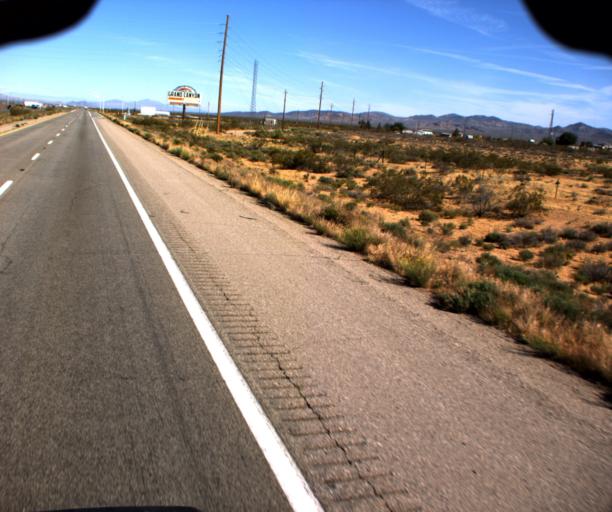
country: US
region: Arizona
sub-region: Mohave County
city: Dolan Springs
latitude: 35.5312
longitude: -114.3533
